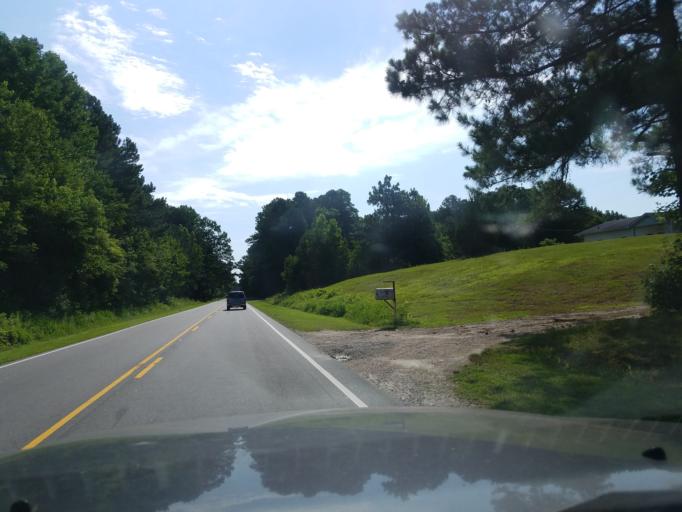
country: US
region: North Carolina
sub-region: Vance County
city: South Henderson
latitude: 36.3268
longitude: -78.4894
